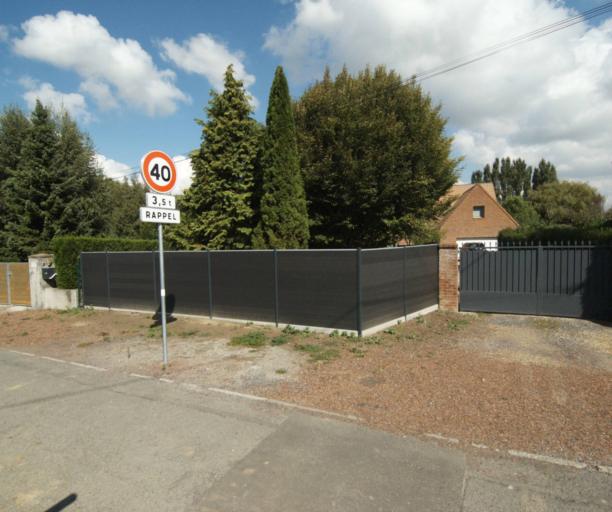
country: FR
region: Nord-Pas-de-Calais
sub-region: Departement du Nord
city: Illies
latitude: 50.5724
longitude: 2.8245
